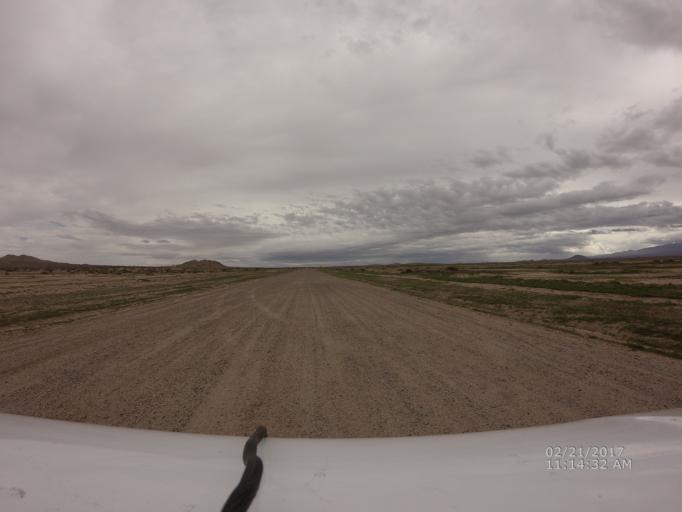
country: US
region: California
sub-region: Los Angeles County
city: Lake Los Angeles
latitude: 34.6459
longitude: -117.8129
